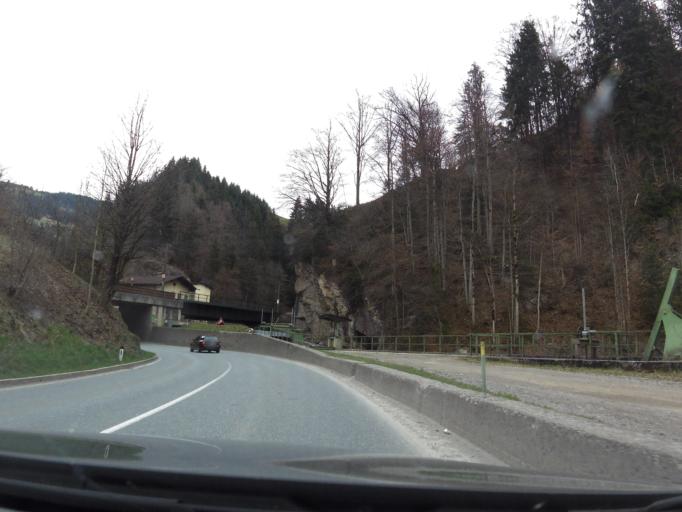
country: AT
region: Tyrol
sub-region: Politischer Bezirk Kitzbuhel
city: Hopfgarten im Brixental
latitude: 47.4376
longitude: 12.1696
